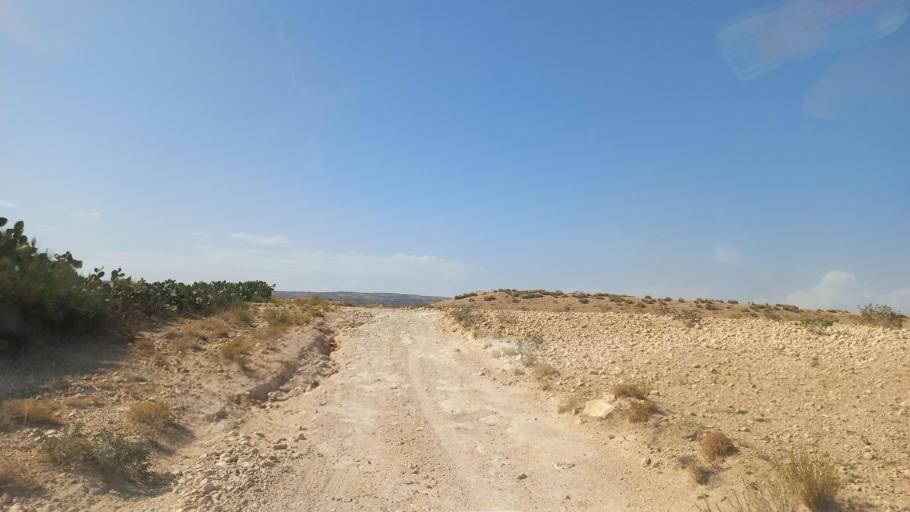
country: TN
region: Al Qasrayn
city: Kasserine
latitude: 35.2793
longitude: 8.9381
